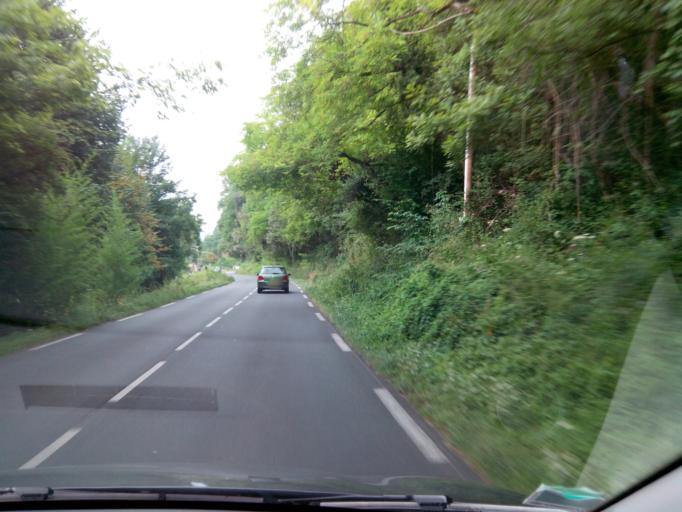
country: FR
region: Aquitaine
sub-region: Departement de la Dordogne
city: Eyvigues-et-Eybenes
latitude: 44.8731
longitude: 1.3662
